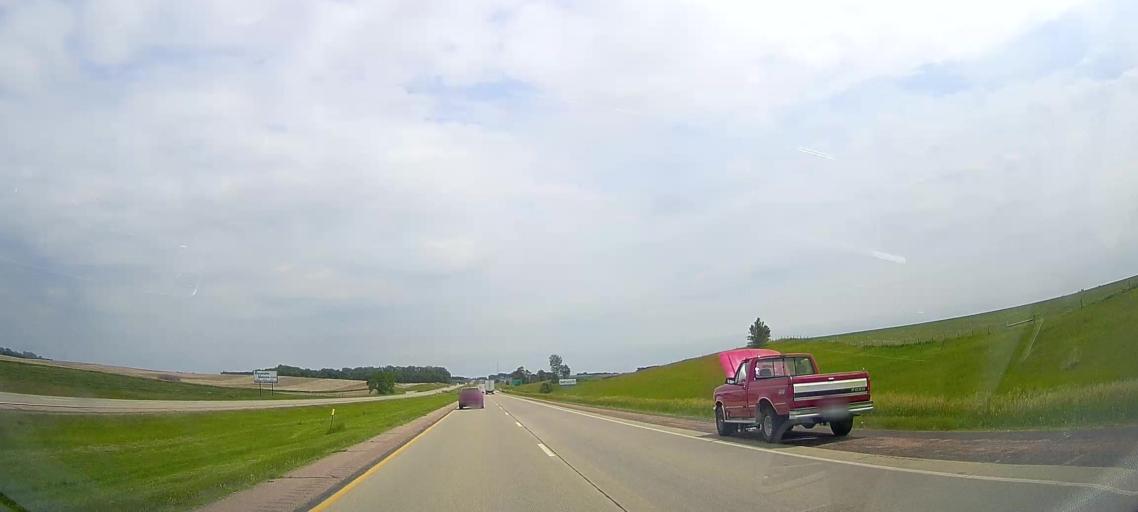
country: US
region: South Dakota
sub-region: Minnehaha County
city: Crooks
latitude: 43.6085
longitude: -96.8454
